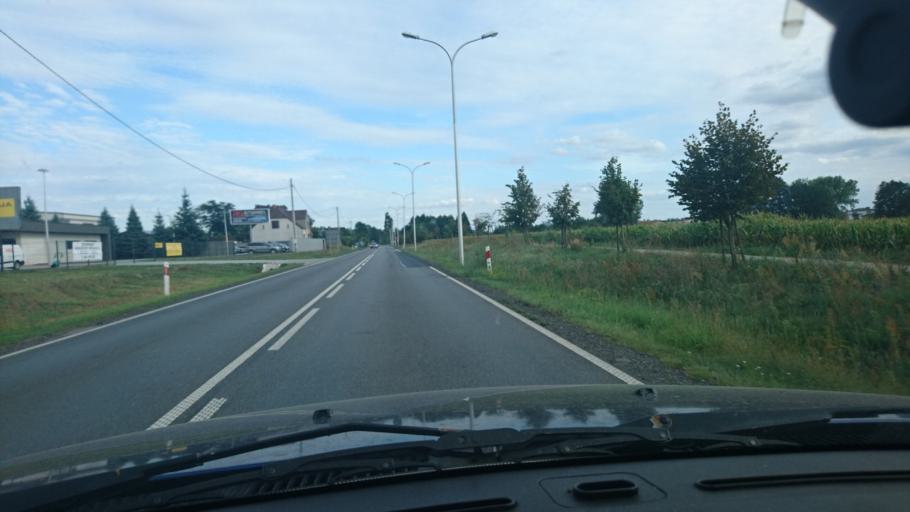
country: PL
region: Greater Poland Voivodeship
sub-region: Powiat kepinski
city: Kepno
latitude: 51.3037
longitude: 17.9916
